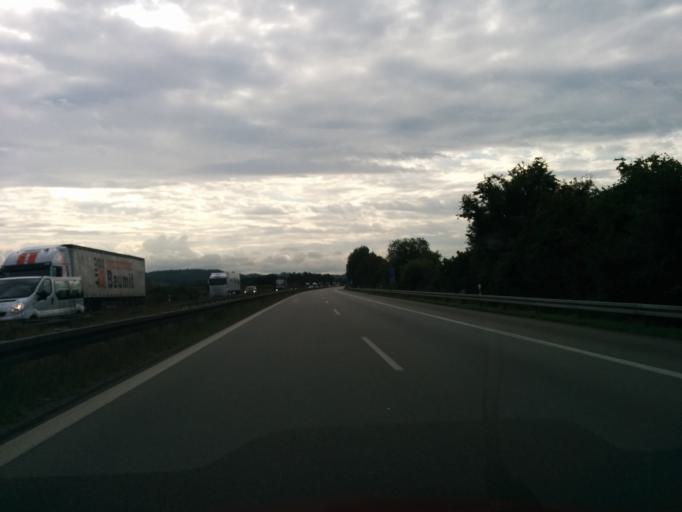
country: DE
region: Bavaria
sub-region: Lower Bavaria
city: Kirchroth
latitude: 48.9628
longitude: 12.5330
